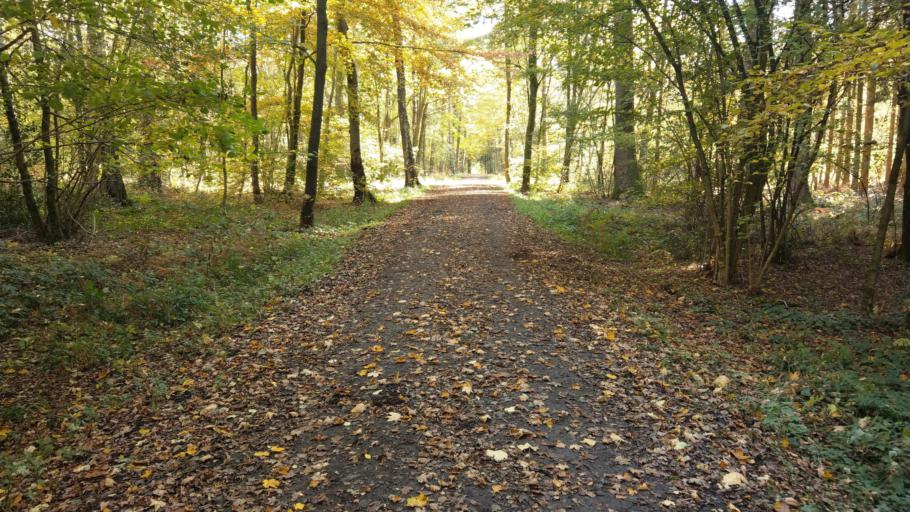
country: BE
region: Wallonia
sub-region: Province de Liege
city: Raeren
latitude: 50.6913
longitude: 6.1261
